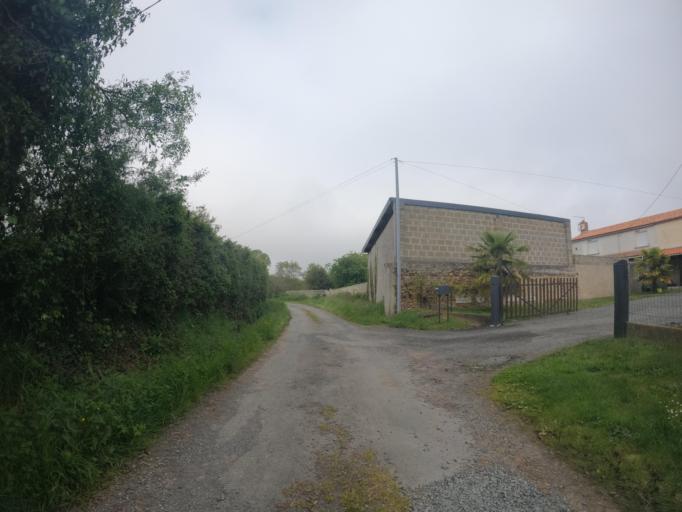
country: FR
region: Poitou-Charentes
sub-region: Departement des Deux-Sevres
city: Saint-Varent
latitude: 46.8827
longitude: -0.3160
